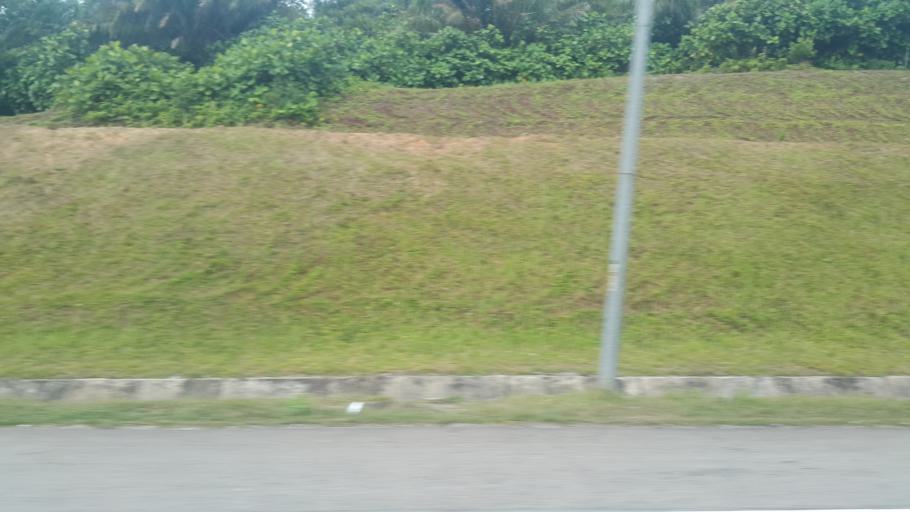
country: MY
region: Johor
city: Pekan Nenas
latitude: 1.3888
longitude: 103.5916
